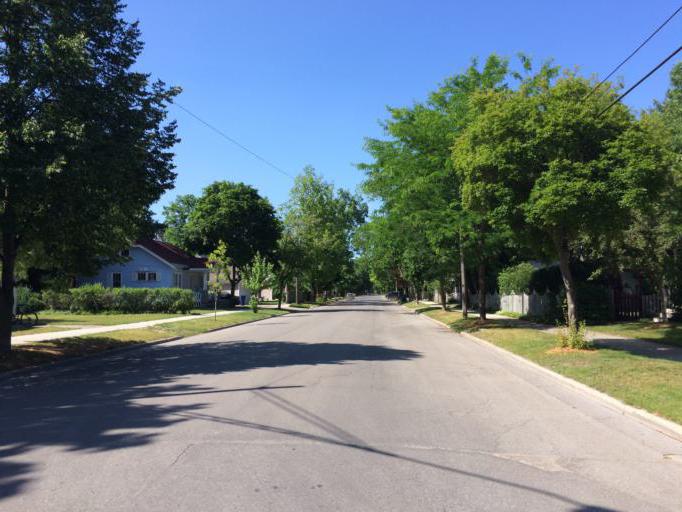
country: US
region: Michigan
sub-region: Grand Traverse County
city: Traverse City
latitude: 44.7558
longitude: -85.6306
